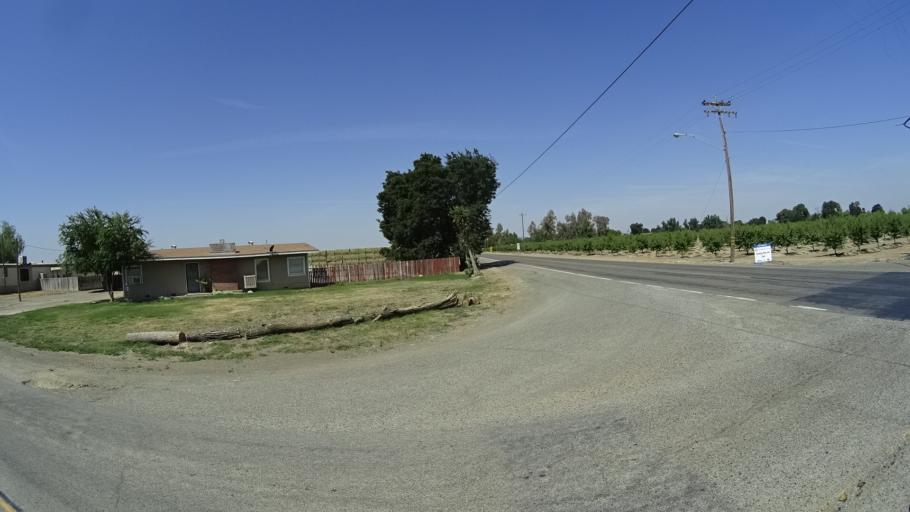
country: US
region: California
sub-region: Kings County
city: Lemoore
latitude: 36.3438
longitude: -119.8512
